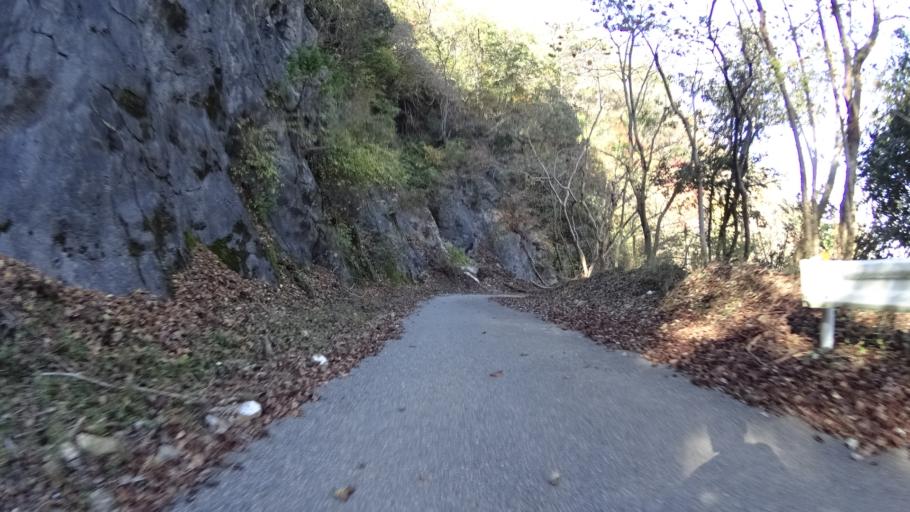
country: JP
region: Kanagawa
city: Atsugi
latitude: 35.5123
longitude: 139.2704
